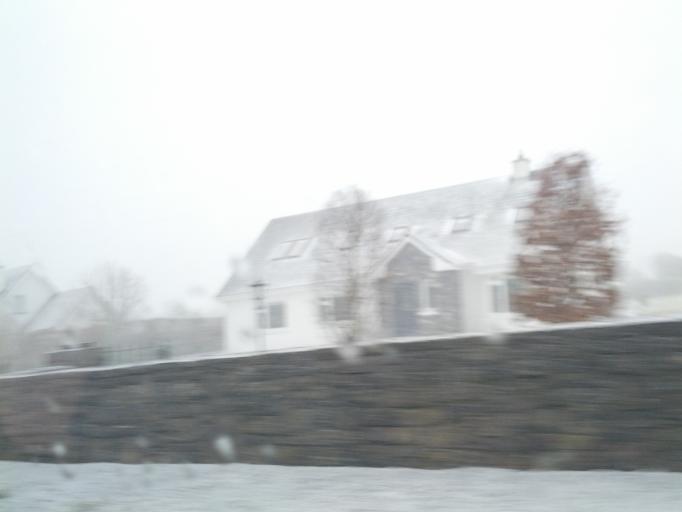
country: IE
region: Connaught
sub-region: County Galway
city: Oranmore
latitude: 53.2011
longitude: -8.9036
